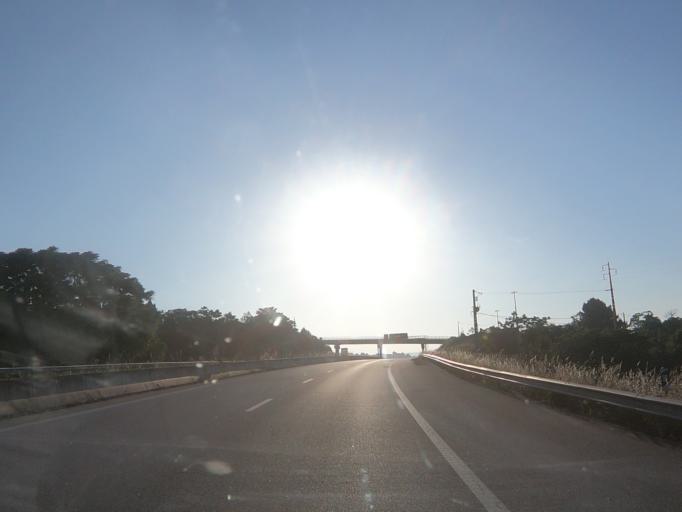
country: PT
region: Guarda
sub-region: Celorico da Beira
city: Celorico da Beira
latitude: 40.6265
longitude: -7.3677
